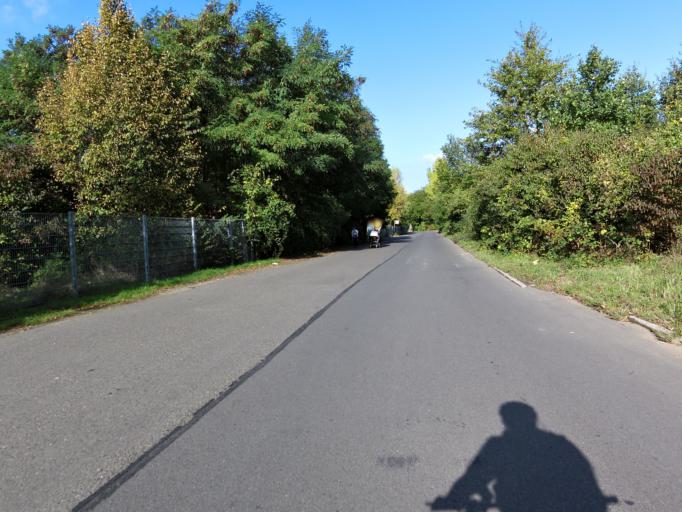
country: DE
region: Saxony
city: Leipzig
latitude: 51.3407
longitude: 12.3401
